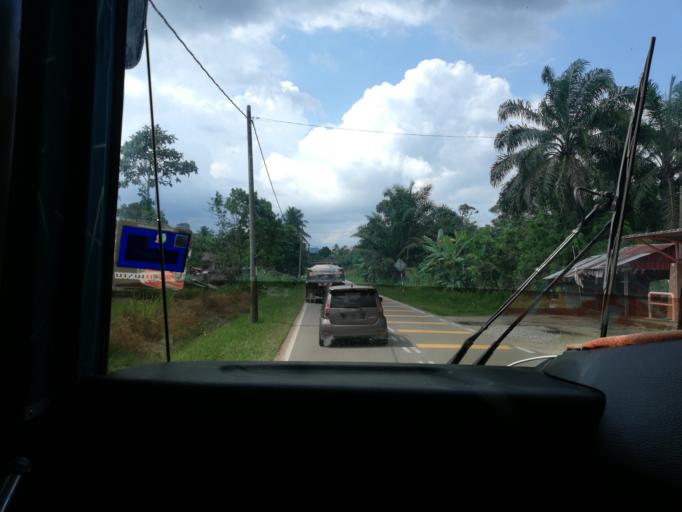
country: MY
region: Penang
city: Nibong Tebal
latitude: 5.2250
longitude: 100.6073
